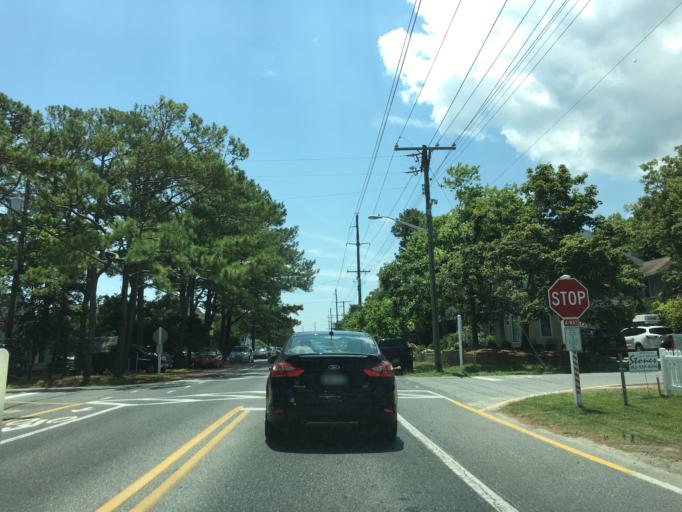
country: US
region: Delaware
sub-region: Sussex County
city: Bethany Beach
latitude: 38.5350
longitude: -75.0570
